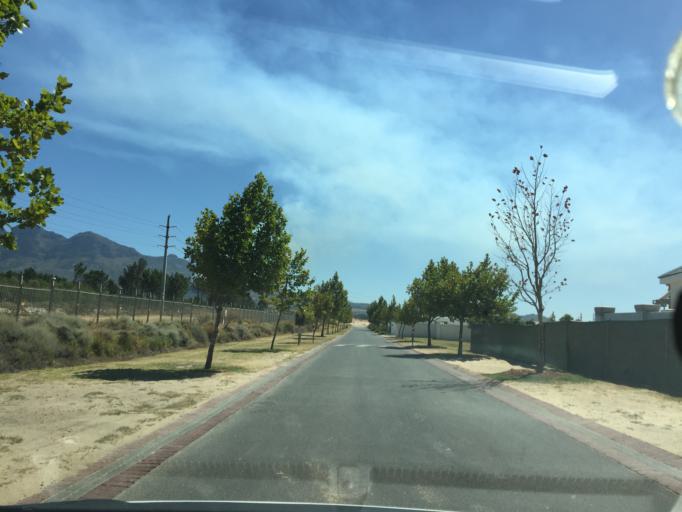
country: ZA
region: Western Cape
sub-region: Cape Winelands District Municipality
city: Paarl
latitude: -33.8080
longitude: 18.9769
